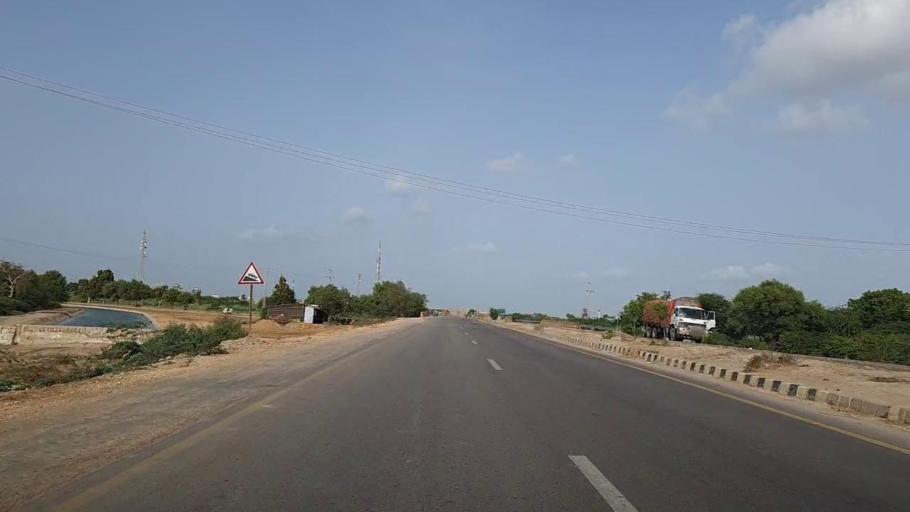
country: PK
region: Sindh
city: Thatta
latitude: 24.7399
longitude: 67.7623
